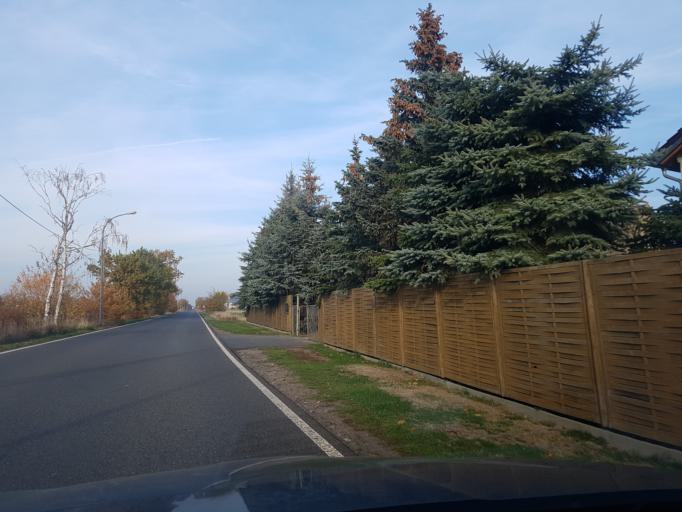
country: DE
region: Brandenburg
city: Falkenberg
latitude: 51.5583
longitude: 13.2270
